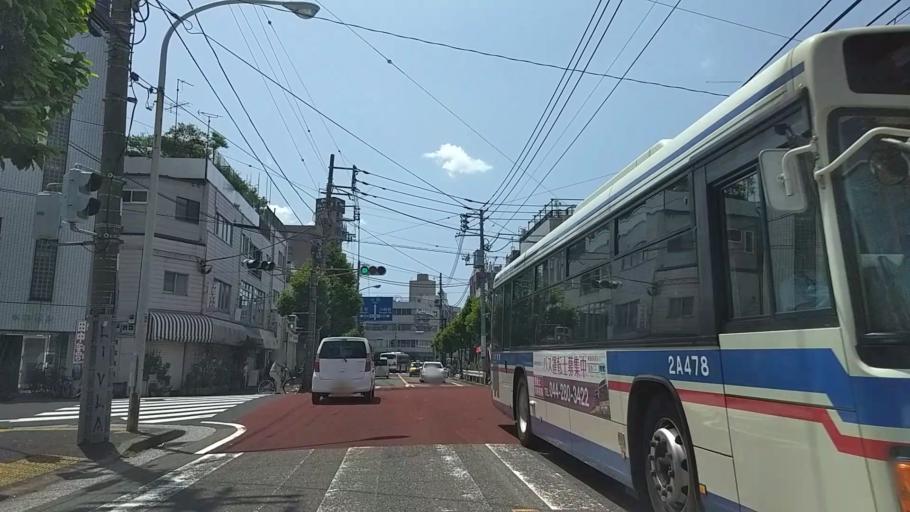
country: JP
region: Kanagawa
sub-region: Kawasaki-shi
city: Kawasaki
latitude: 35.5195
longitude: 139.7184
